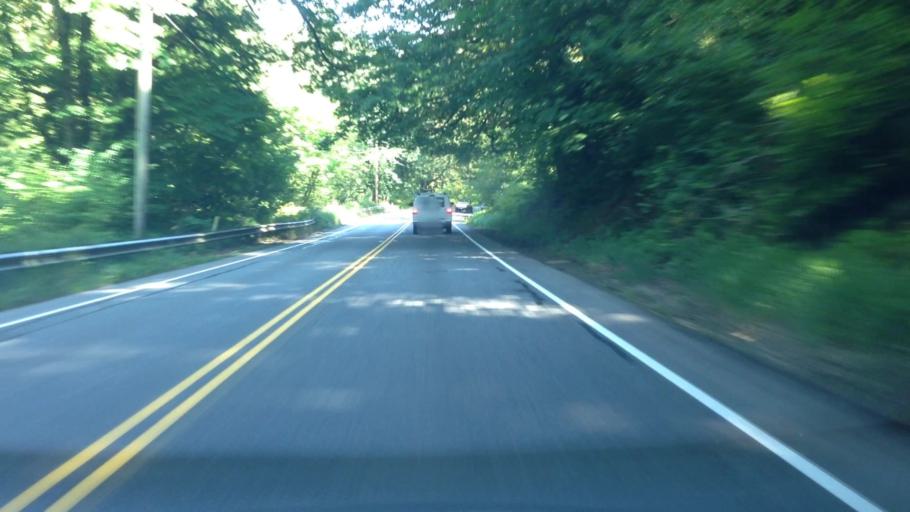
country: US
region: Washington
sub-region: King County
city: Duvall
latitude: 47.7495
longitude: -122.0156
